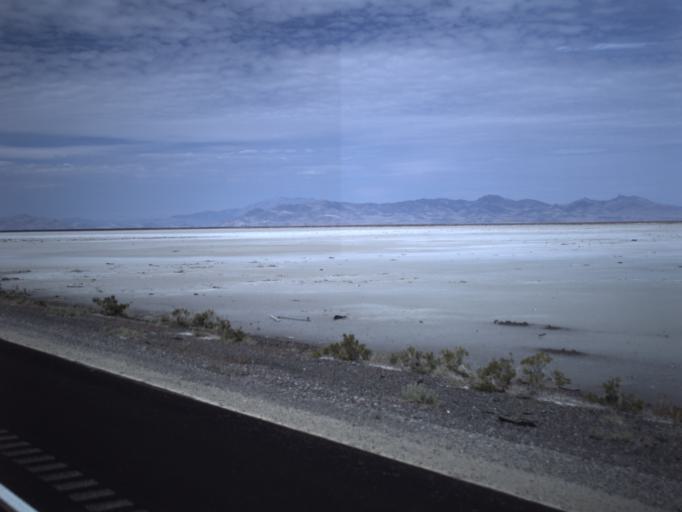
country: US
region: Utah
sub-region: Tooele County
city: Wendover
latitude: 40.7325
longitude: -113.5303
